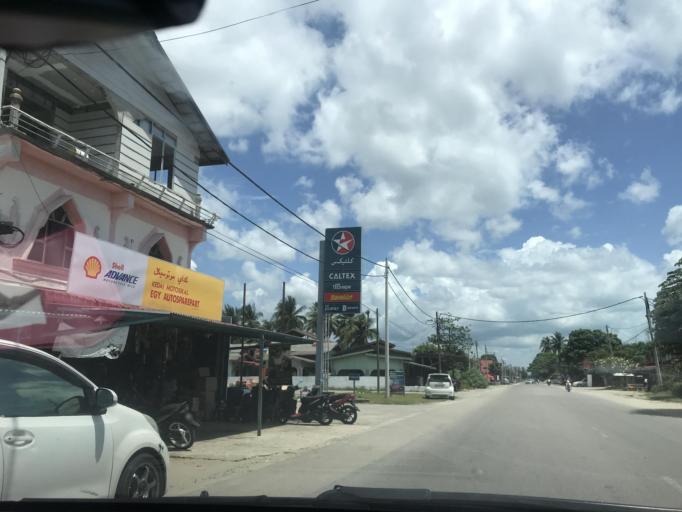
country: TH
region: Narathiwat
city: Tak Bai
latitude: 6.2264
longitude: 102.1021
